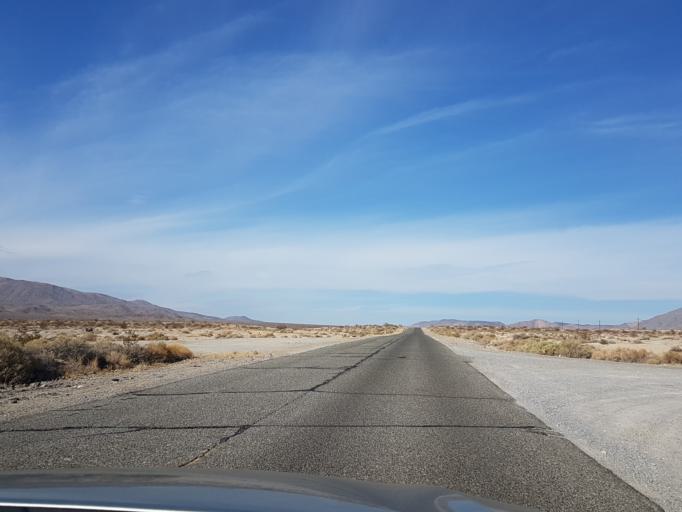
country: US
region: California
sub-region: San Bernardino County
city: Searles Valley
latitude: 35.8448
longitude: -117.3364
